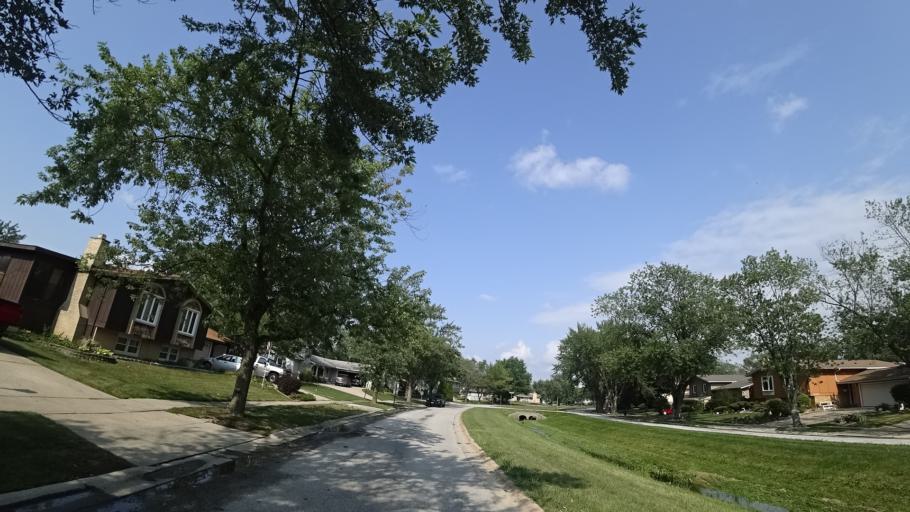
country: US
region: Illinois
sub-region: Cook County
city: Oak Forest
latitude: 41.6118
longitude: -87.7727
